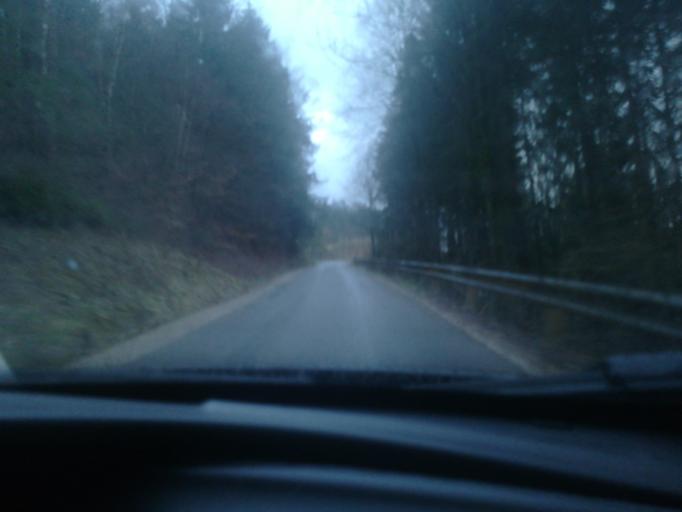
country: AT
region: Upper Austria
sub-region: Politischer Bezirk Perg
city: Perg
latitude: 48.3000
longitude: 14.6305
